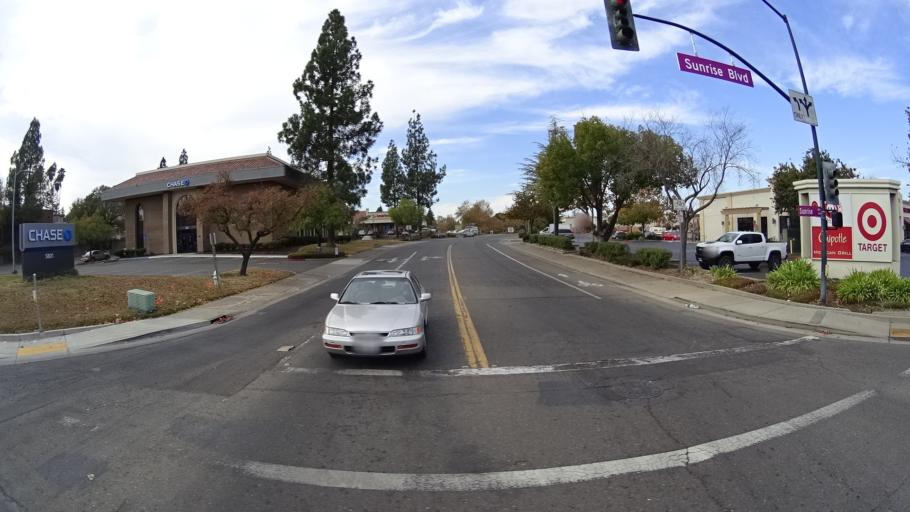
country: US
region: California
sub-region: Sacramento County
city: Fair Oaks
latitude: 38.6717
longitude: -121.2717
